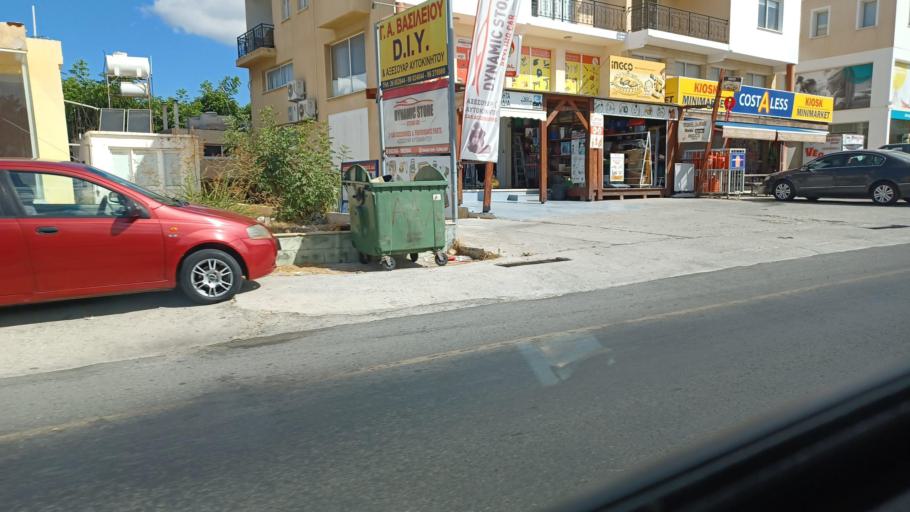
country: CY
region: Pafos
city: Empa
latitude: 34.7958
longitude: 32.4384
